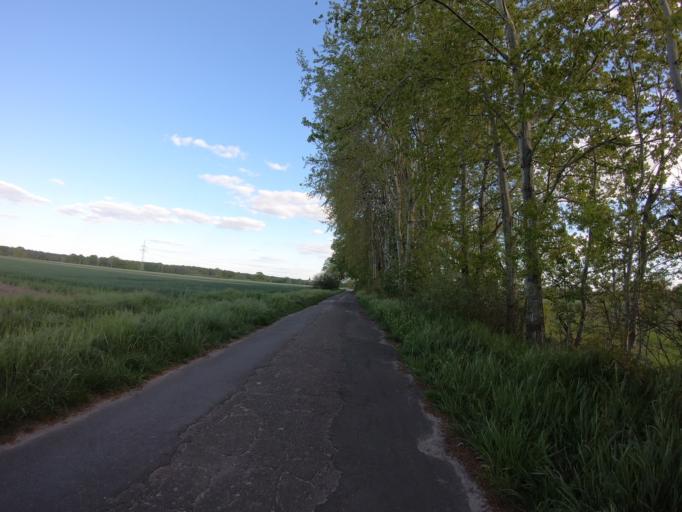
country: DE
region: Lower Saxony
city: Gifhorn
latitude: 52.5020
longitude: 10.5466
